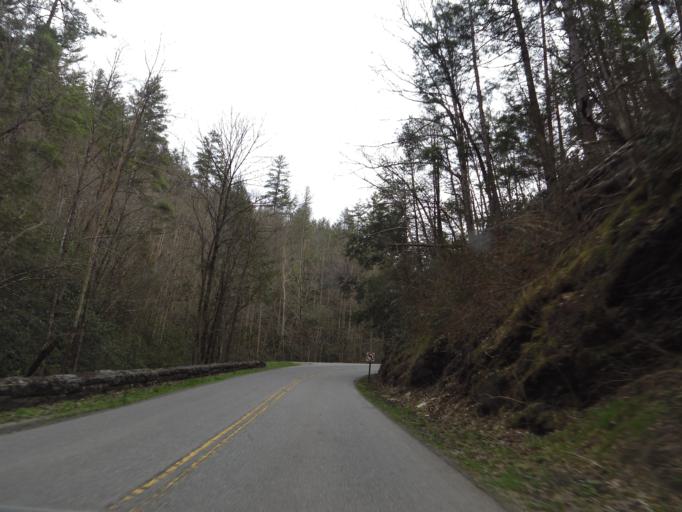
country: US
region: Tennessee
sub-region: Blount County
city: Wildwood
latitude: 35.6381
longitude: -83.7226
